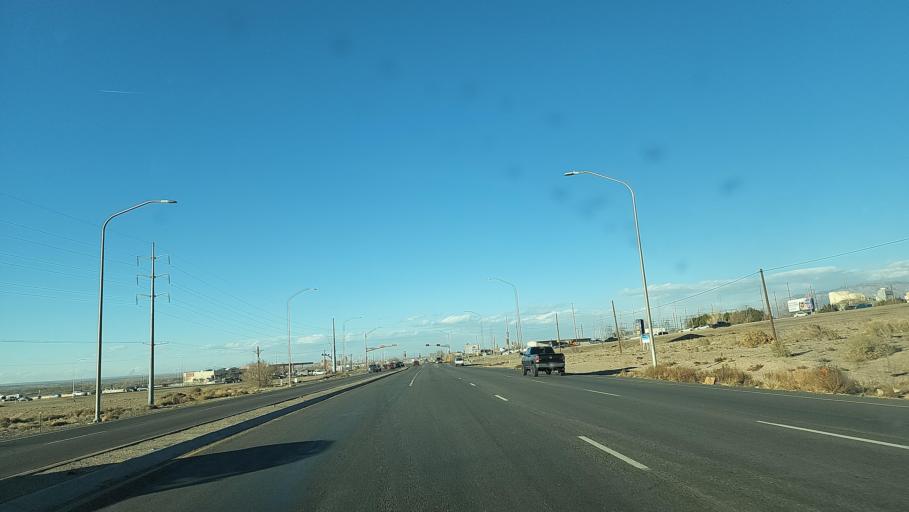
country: US
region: New Mexico
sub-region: Bernalillo County
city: South Valley
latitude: 35.0233
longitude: -106.6467
